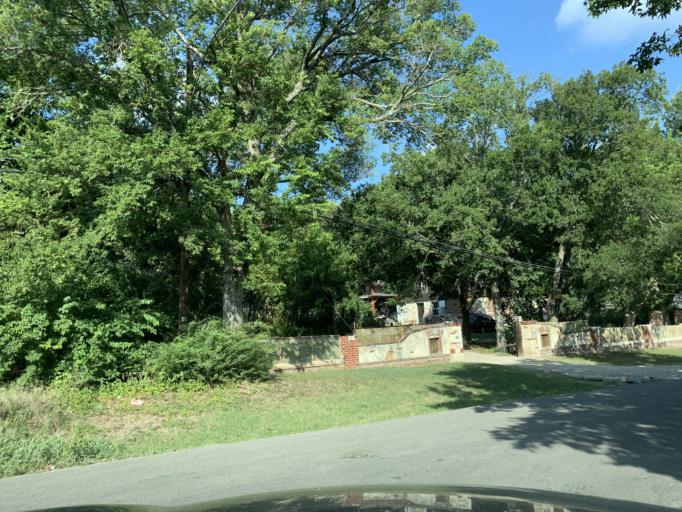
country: US
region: Texas
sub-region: Dallas County
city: Hutchins
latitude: 32.6761
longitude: -96.7818
